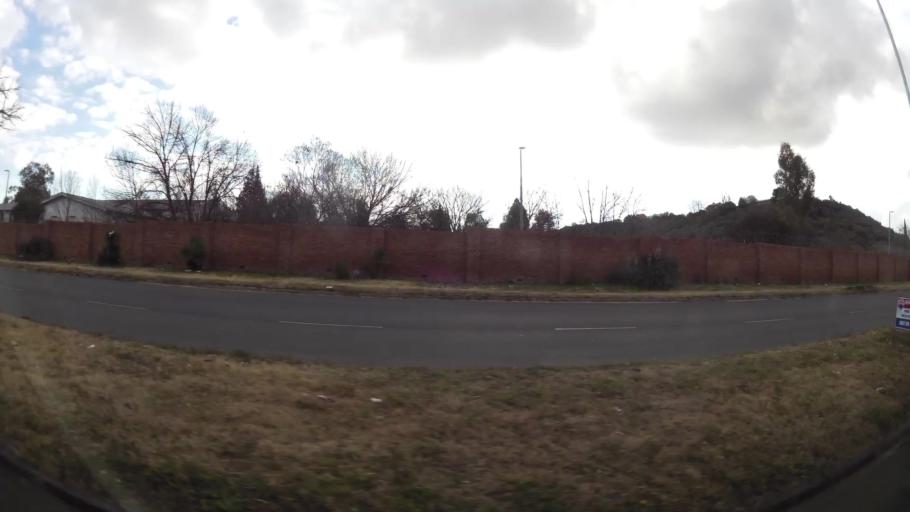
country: ZA
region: Orange Free State
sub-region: Mangaung Metropolitan Municipality
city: Bloemfontein
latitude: -29.0918
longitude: 26.2036
